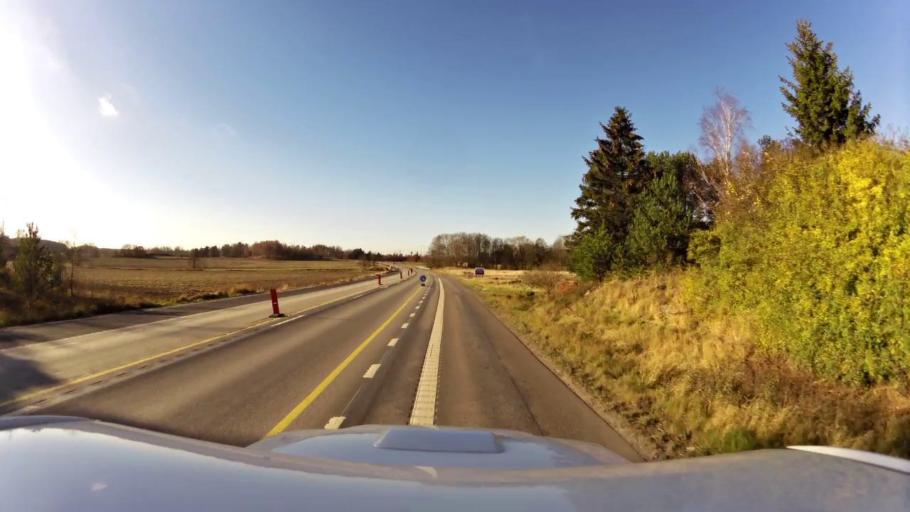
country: SE
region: OEstergoetland
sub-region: Linkopings Kommun
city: Linghem
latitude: 58.4379
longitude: 15.7482
